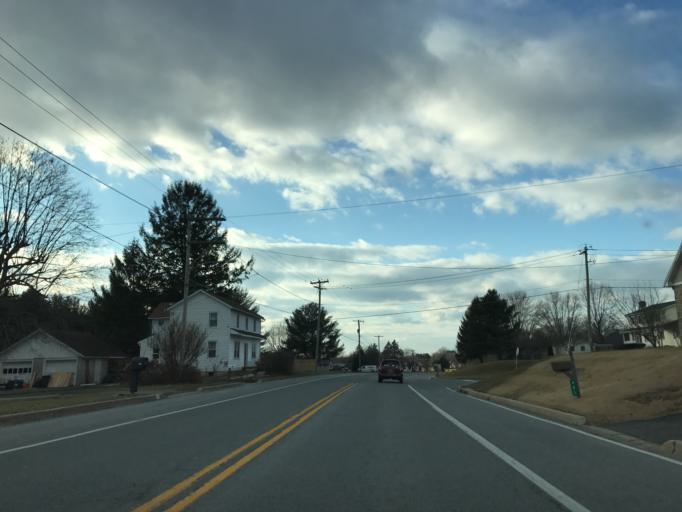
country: US
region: Maryland
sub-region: Cecil County
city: Rising Sun
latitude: 39.6908
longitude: -76.0478
